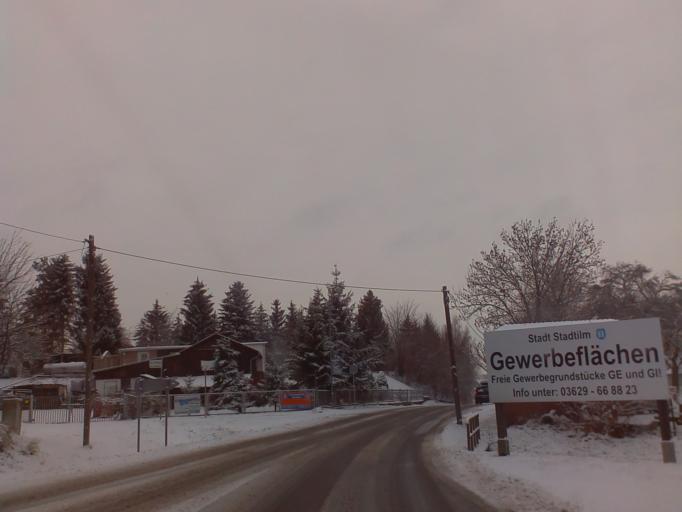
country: DE
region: Thuringia
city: Stadtilm
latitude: 50.7733
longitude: 11.0928
